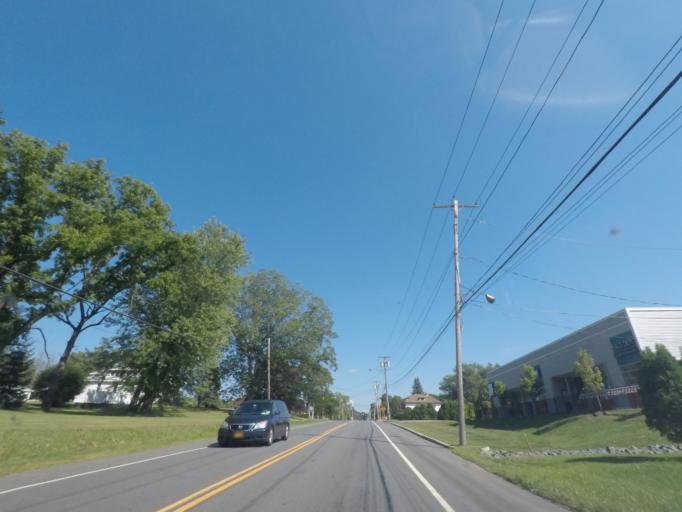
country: US
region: New York
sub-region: Albany County
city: Roessleville
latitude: 42.7376
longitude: -73.7733
